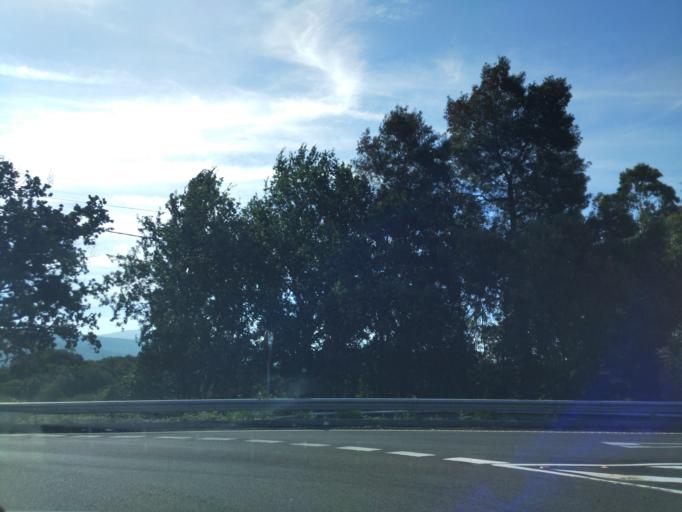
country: ES
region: Galicia
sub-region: Provincia da Coruna
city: Padron
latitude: 42.7256
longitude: -8.6755
